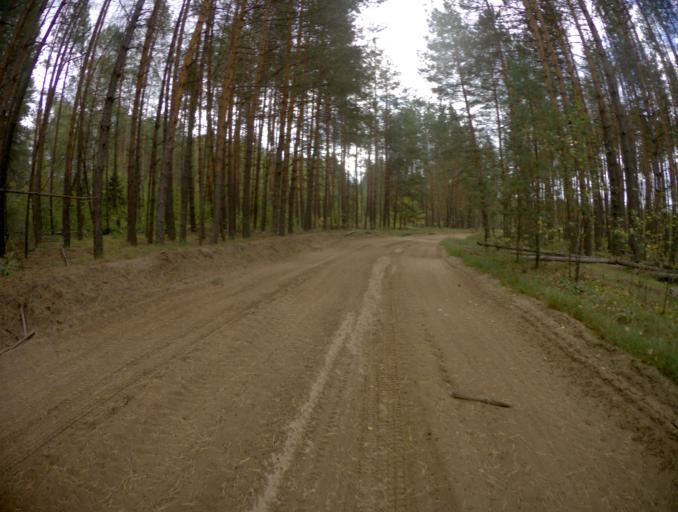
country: RU
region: Vladimir
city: Petushki
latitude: 55.8789
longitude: 39.5306
